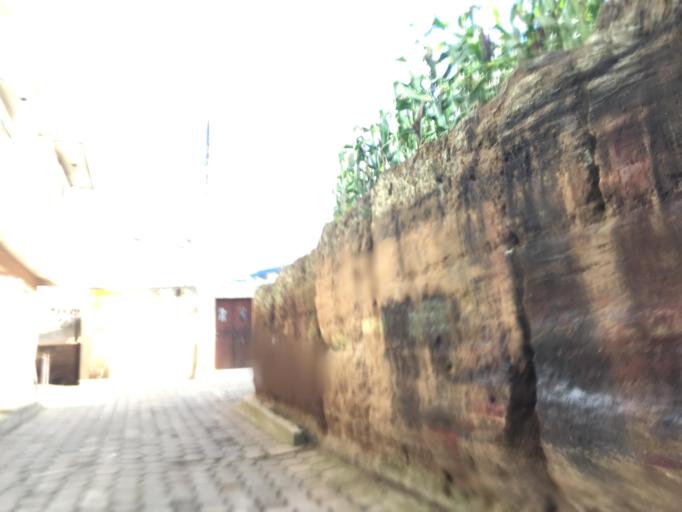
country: GT
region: Totonicapan
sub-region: Municipio de Totonicapan
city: Totonicapan
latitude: 14.9104
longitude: -91.3646
